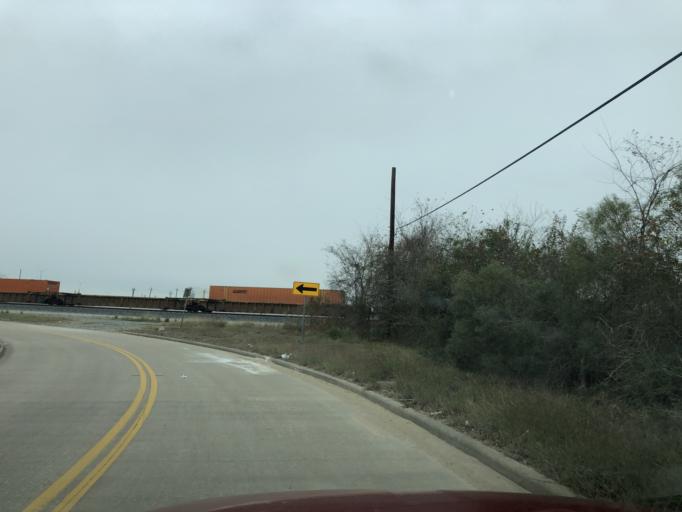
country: US
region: Texas
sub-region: Fort Bend County
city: Missouri City
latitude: 29.6268
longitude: -95.5203
